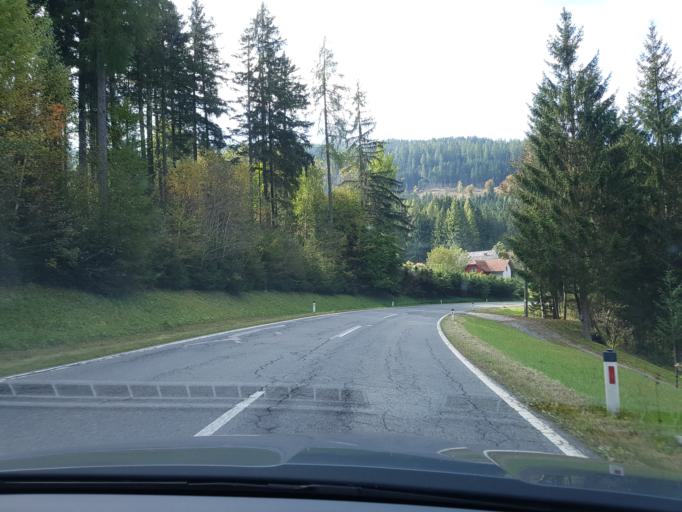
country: AT
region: Carinthia
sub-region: Politischer Bezirk Feldkirchen
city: Gnesau
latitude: 46.7695
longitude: 13.9948
